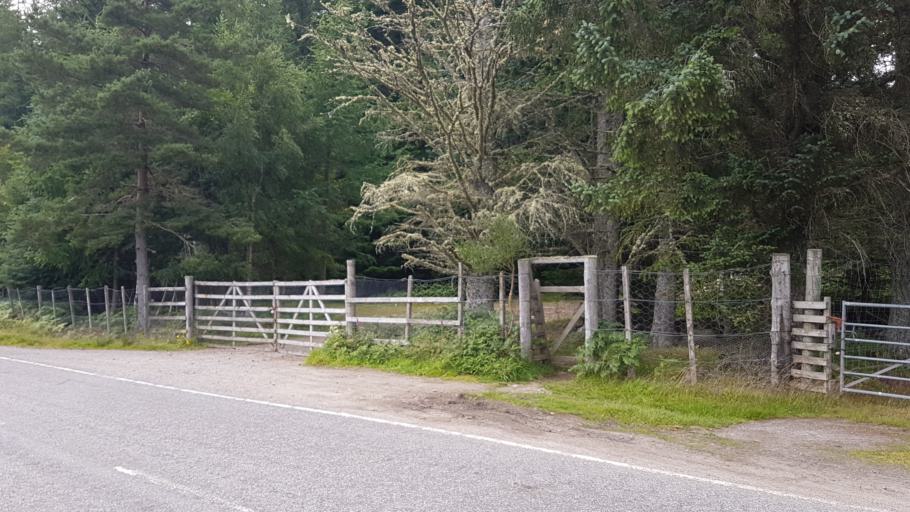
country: GB
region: Scotland
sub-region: Highland
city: Beauly
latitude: 57.2026
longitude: -4.5075
